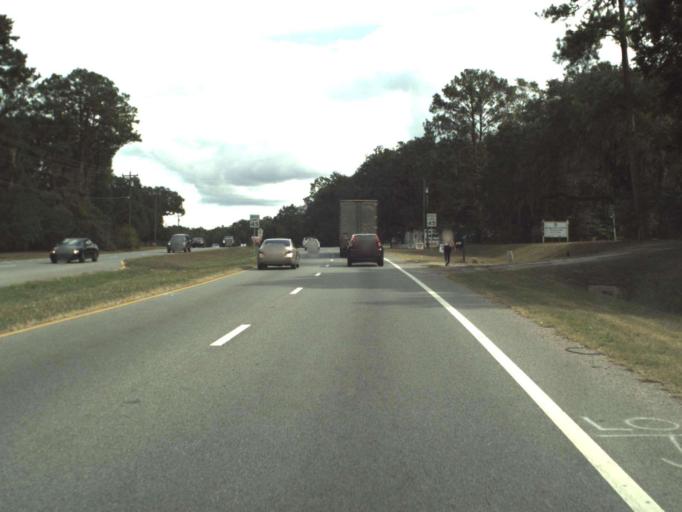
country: US
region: Florida
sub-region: Leon County
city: Tallahassee
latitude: 30.5098
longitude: -84.3408
